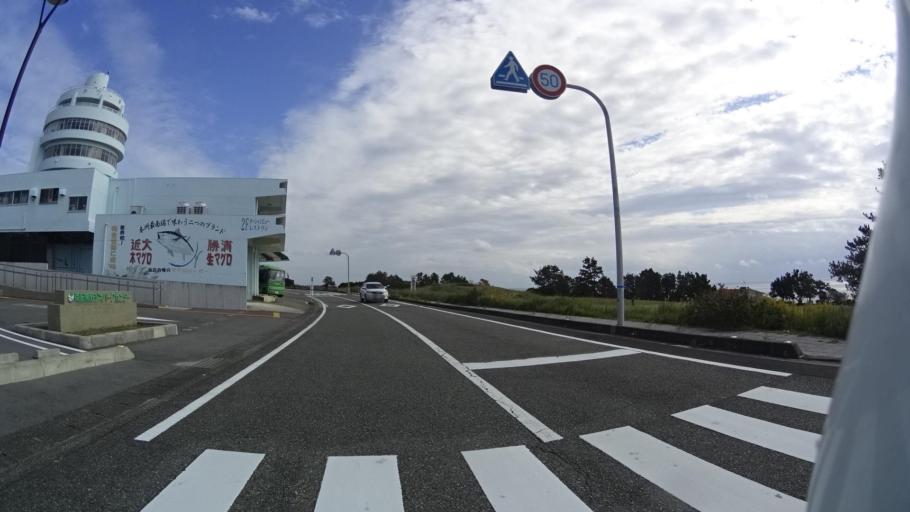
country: JP
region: Wakayama
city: Shingu
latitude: 33.4373
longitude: 135.7608
